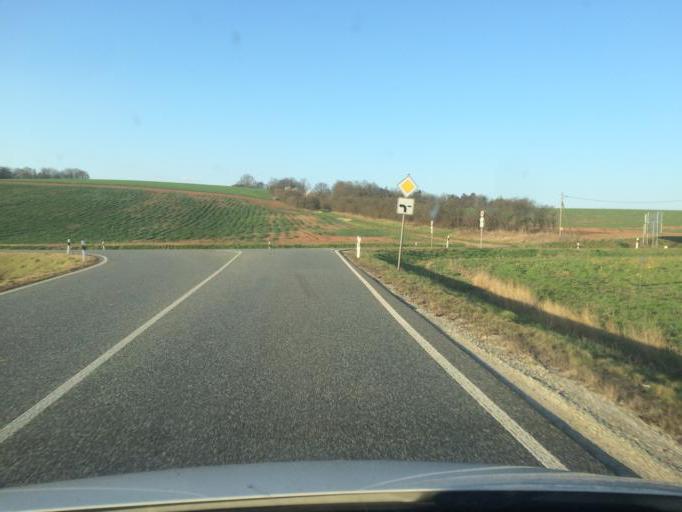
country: DE
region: Thuringia
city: Wipperdorf
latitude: 51.5102
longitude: 10.6950
